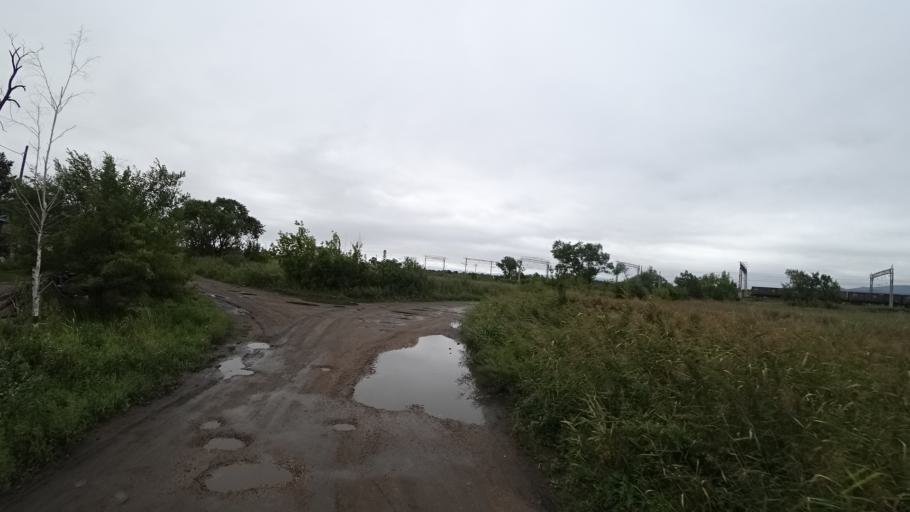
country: RU
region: Primorskiy
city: Chernigovka
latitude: 44.3431
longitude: 132.5352
